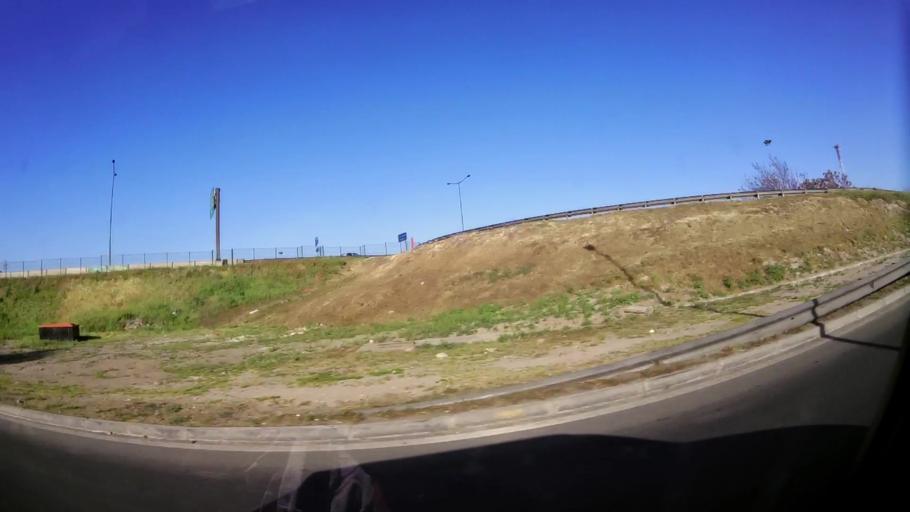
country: CL
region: Santiago Metropolitan
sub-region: Provincia de Santiago
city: Lo Prado
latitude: -33.4875
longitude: -70.7518
